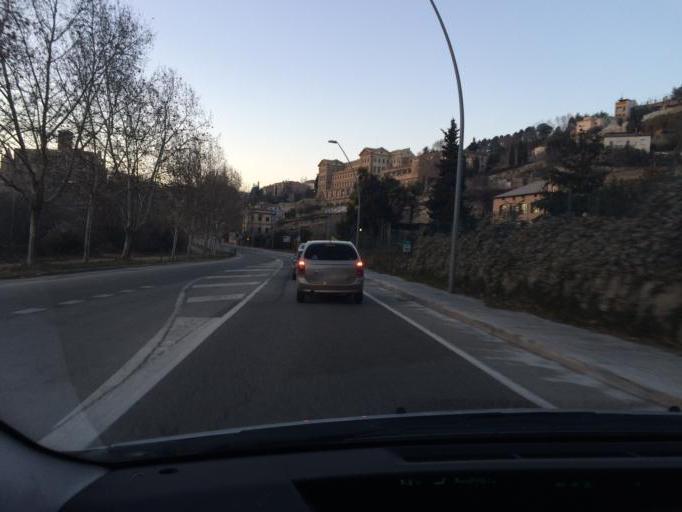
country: ES
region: Catalonia
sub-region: Provincia de Barcelona
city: Manresa
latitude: 41.7189
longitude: 1.8327
